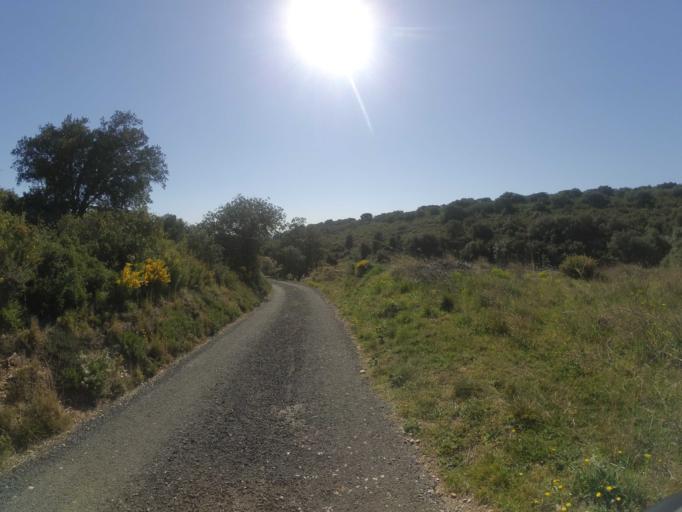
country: FR
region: Languedoc-Roussillon
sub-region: Departement des Pyrenees-Orientales
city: Baixas
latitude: 42.7613
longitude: 2.7814
